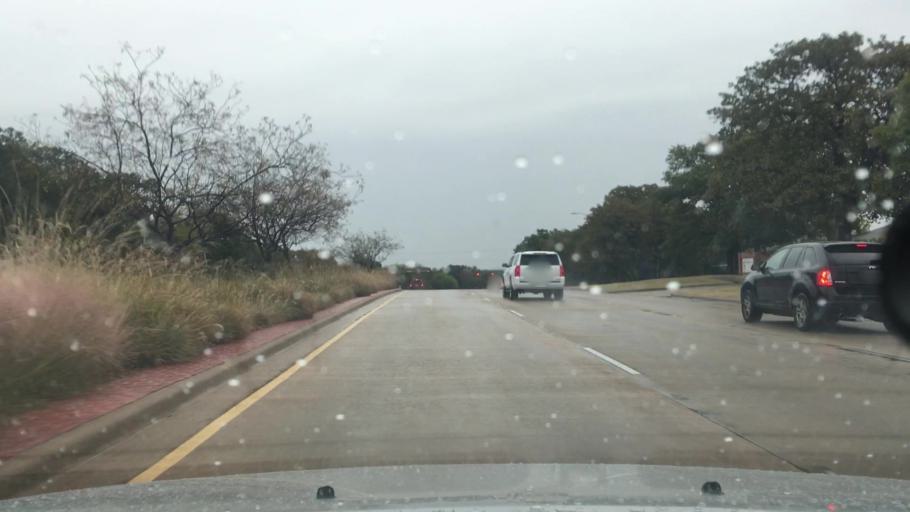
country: US
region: Texas
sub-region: Denton County
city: Denton
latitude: 33.2352
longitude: -97.1088
